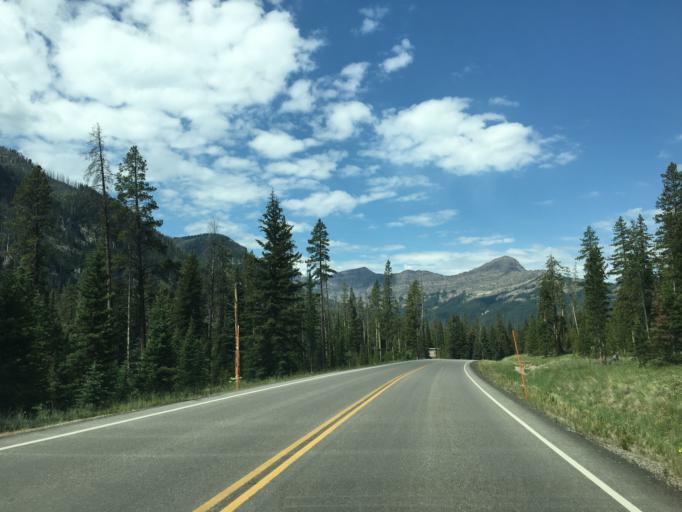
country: US
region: Montana
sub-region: Stillwater County
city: Absarokee
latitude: 45.0036
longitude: -109.9985
